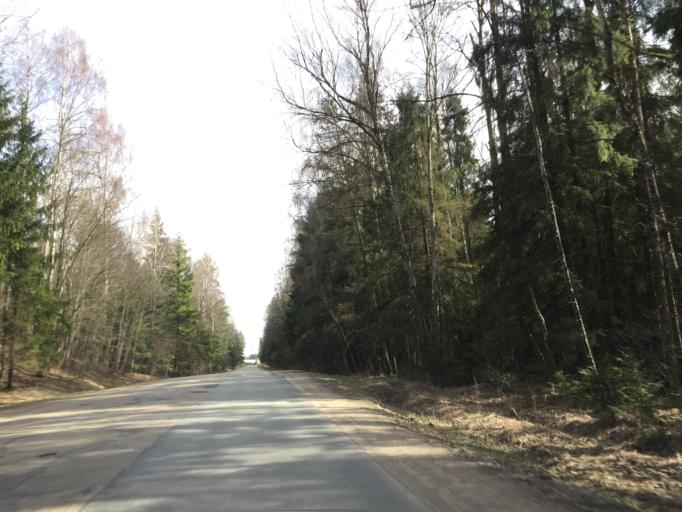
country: LV
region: Ogre
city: Ogre
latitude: 56.8336
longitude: 24.5833
